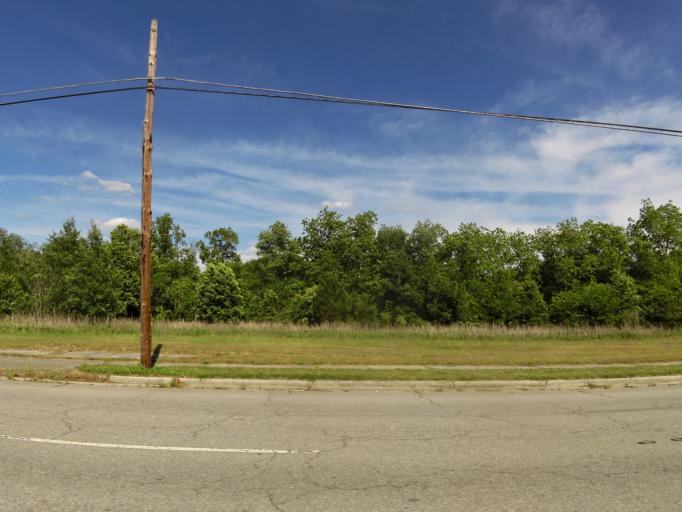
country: US
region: South Carolina
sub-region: Bamberg County
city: Denmark
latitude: 33.3123
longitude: -81.1439
